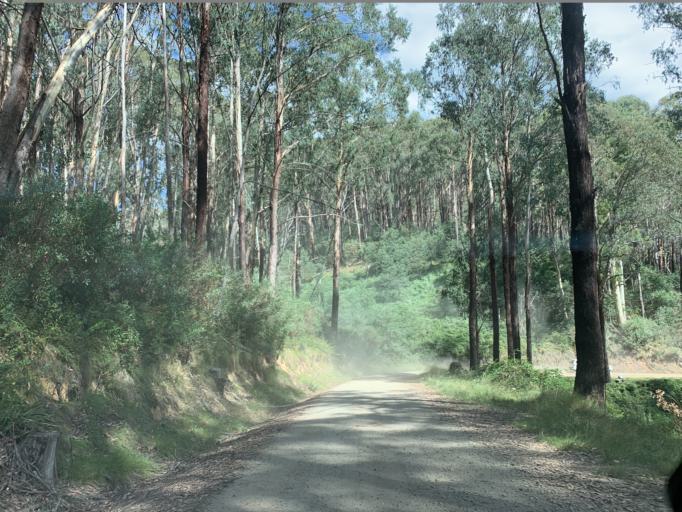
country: AU
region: Victoria
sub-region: Mansfield
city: Mansfield
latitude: -37.0916
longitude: 146.5412
